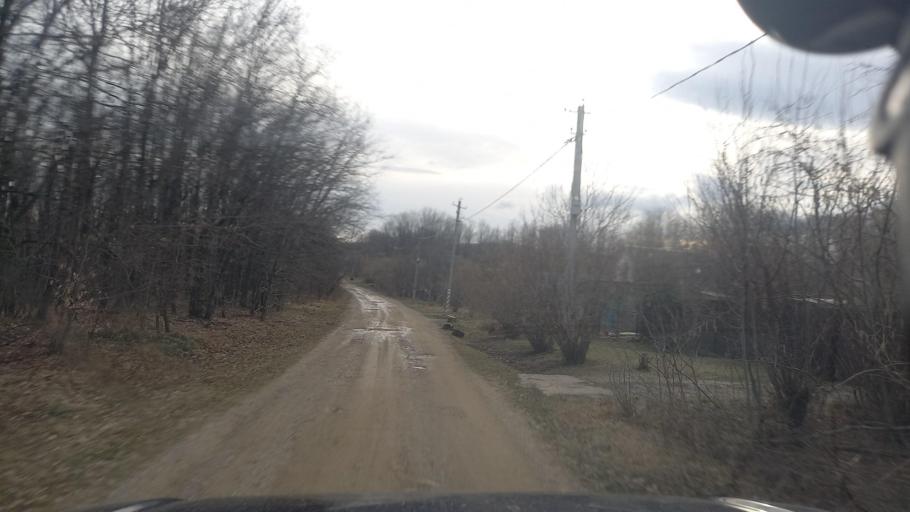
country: RU
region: Krasnodarskiy
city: Goryachiy Klyuch
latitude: 44.6974
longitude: 39.0216
